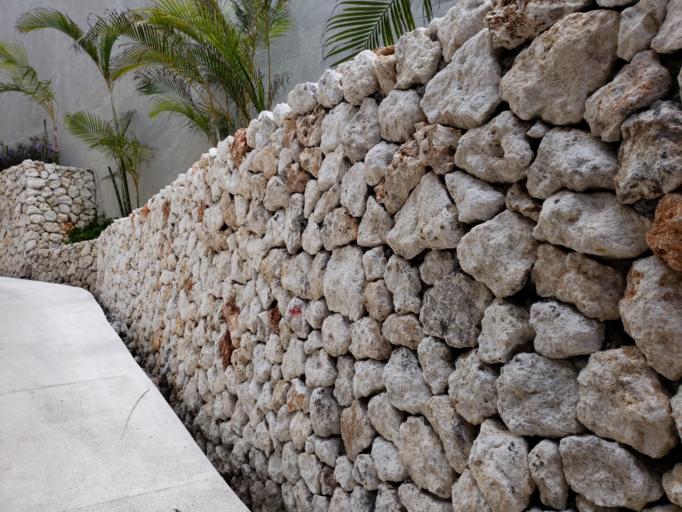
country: ID
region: Bali
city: Kangin
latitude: -8.8459
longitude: 115.1293
